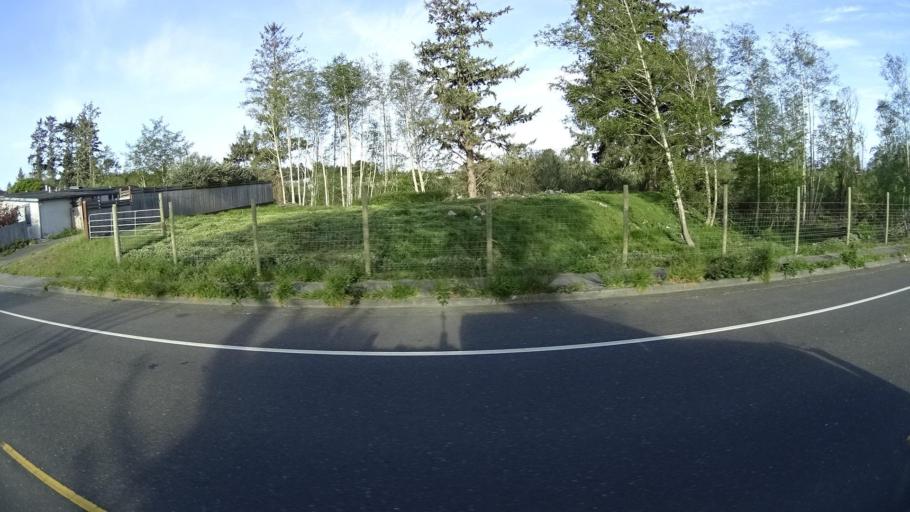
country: US
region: California
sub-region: Humboldt County
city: Humboldt Hill
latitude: 40.7350
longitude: -124.2021
